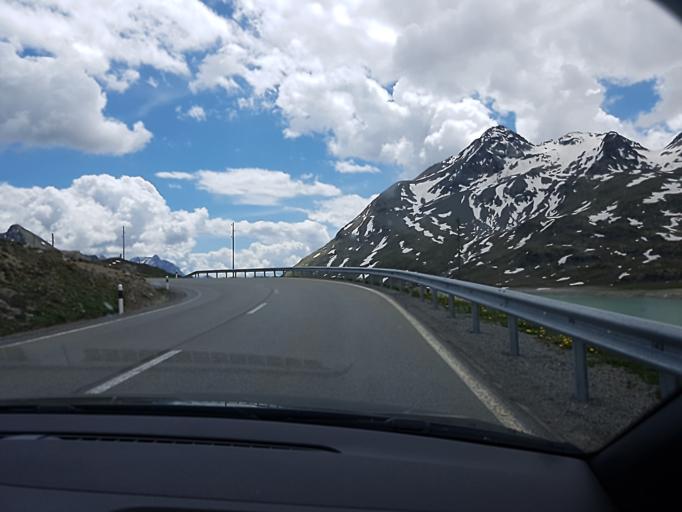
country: CH
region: Grisons
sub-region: Bernina District
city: Poschiavo
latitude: 46.4164
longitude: 10.0134
